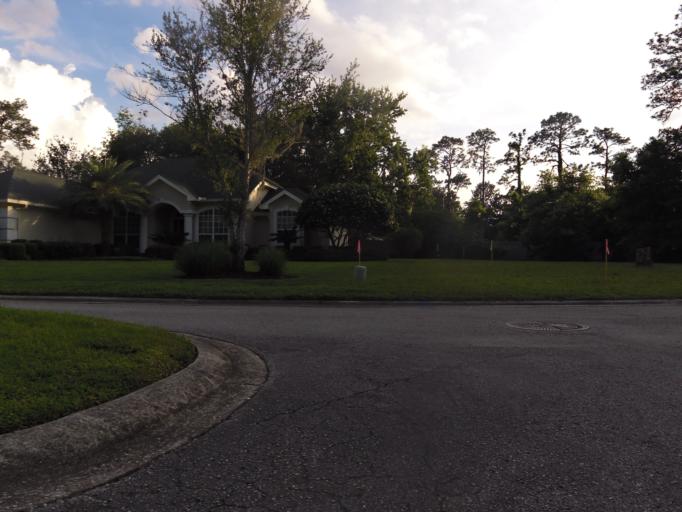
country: US
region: Florida
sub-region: Clay County
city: Orange Park
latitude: 30.2103
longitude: -81.6204
